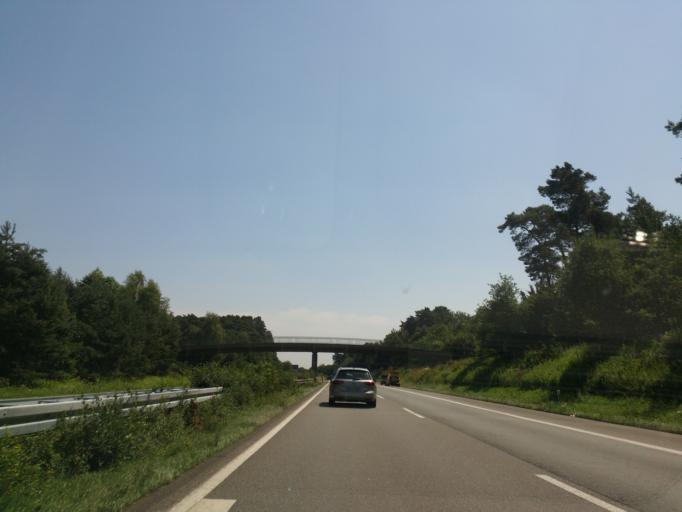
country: DE
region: North Rhine-Westphalia
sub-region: Regierungsbezirk Detmold
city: Verl
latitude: 51.9319
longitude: 8.5747
